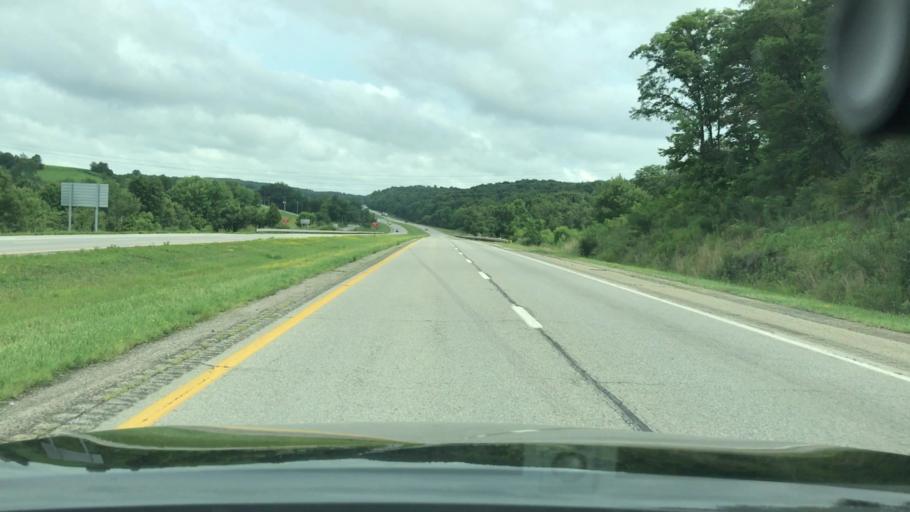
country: US
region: Ohio
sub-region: Jackson County
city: Jackson
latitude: 39.0347
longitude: -82.5993
